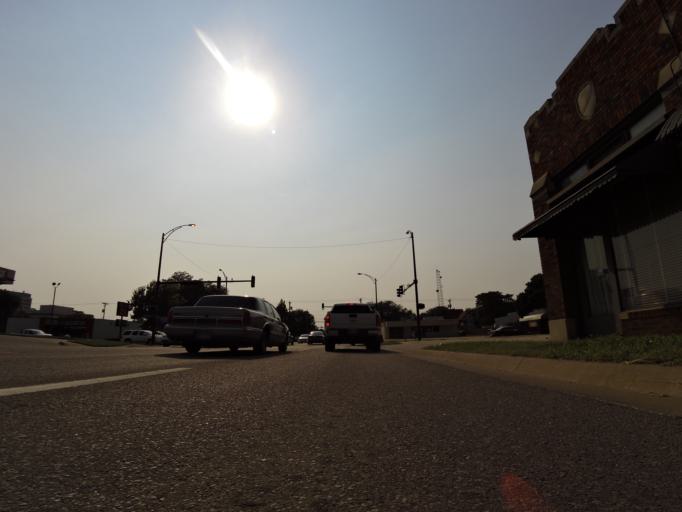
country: US
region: Kansas
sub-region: Sedgwick County
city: Wichita
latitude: 37.6976
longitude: -97.3350
